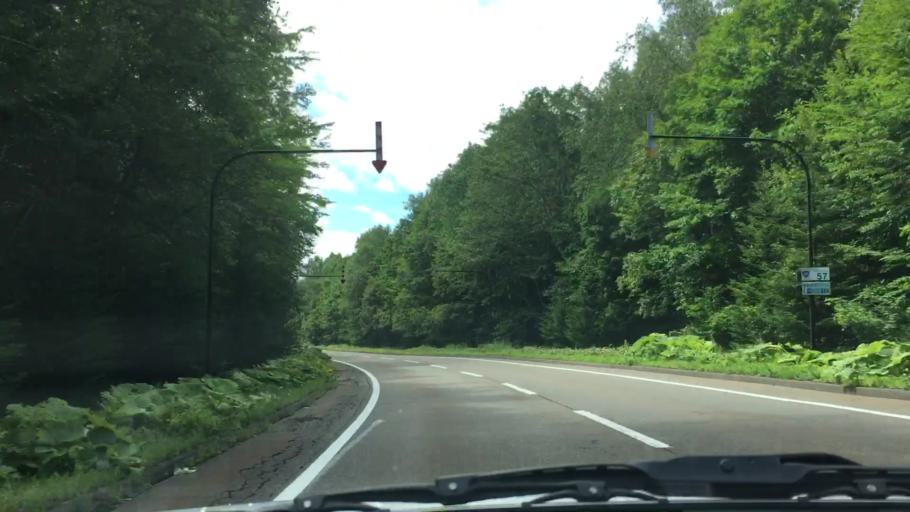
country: JP
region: Hokkaido
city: Kitami
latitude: 43.3987
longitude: 143.9263
